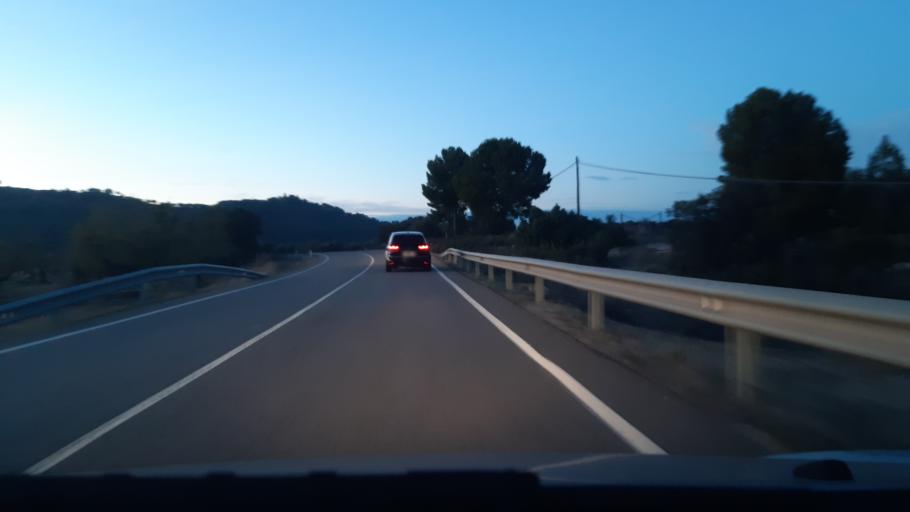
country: ES
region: Aragon
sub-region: Provincia de Teruel
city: Calaceite
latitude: 40.9999
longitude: 0.1949
